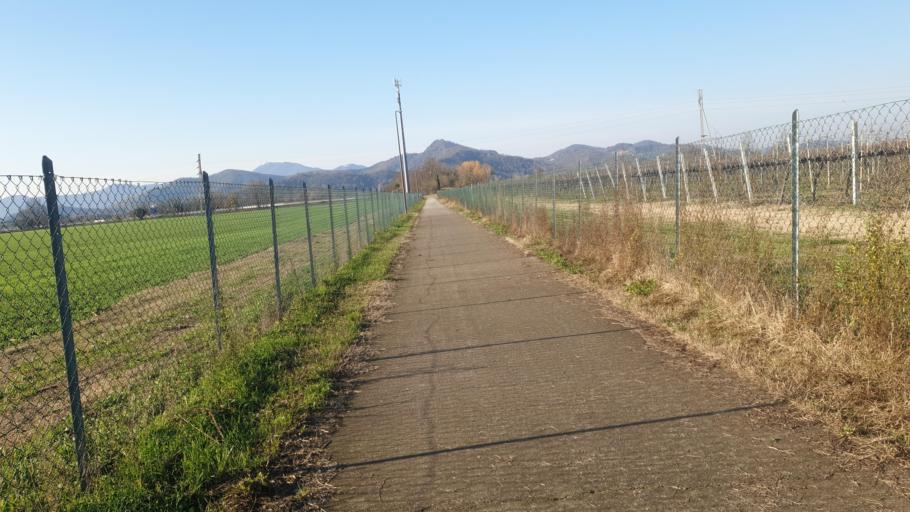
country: IT
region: Veneto
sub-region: Provincia di Padova
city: Carrara San Giorgio
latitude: 45.2963
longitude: 11.8143
